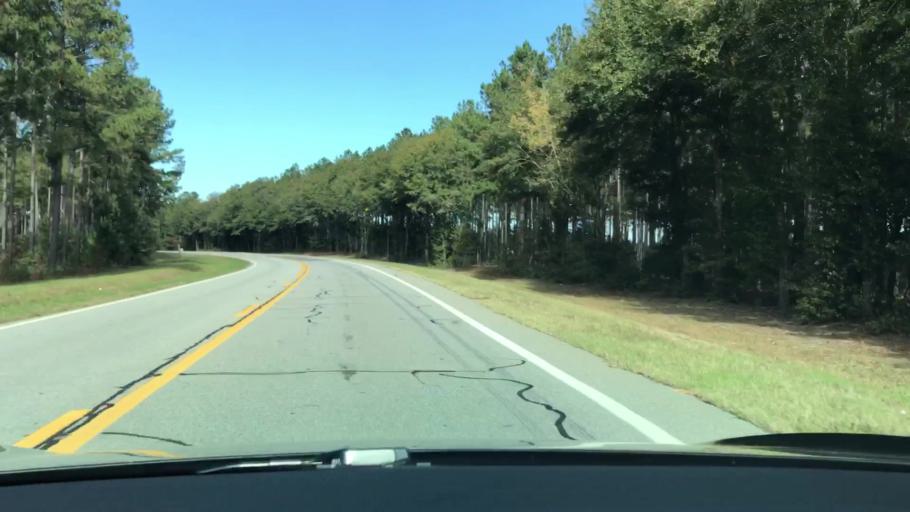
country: US
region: Georgia
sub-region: Warren County
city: Warrenton
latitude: 33.3527
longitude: -82.5869
